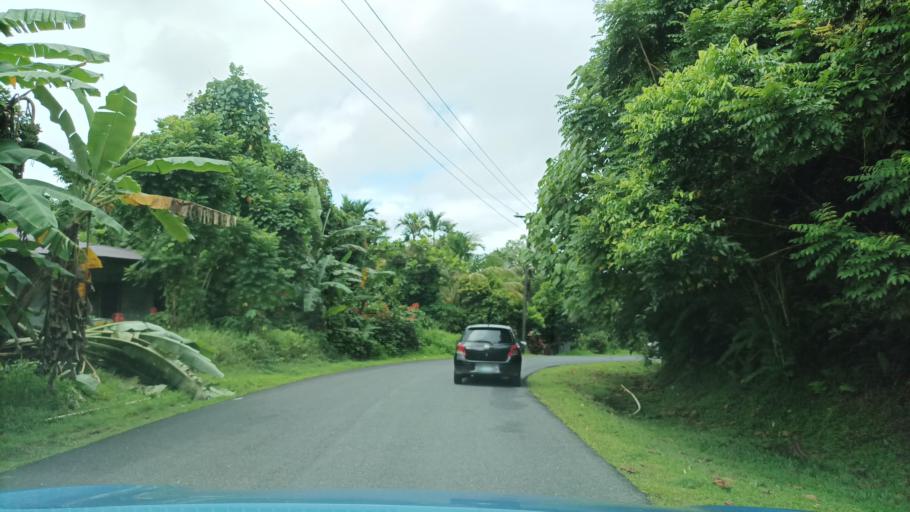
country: FM
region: Pohnpei
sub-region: Sokehs Municipality
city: Palikir - National Government Center
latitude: 6.9252
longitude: 158.1726
